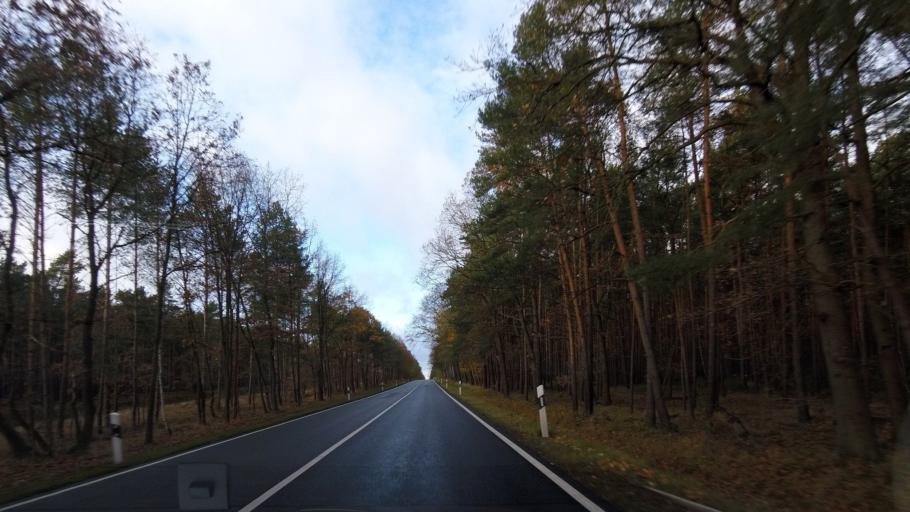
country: DE
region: Brandenburg
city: Treuenbrietzen
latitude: 52.0454
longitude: 12.9184
